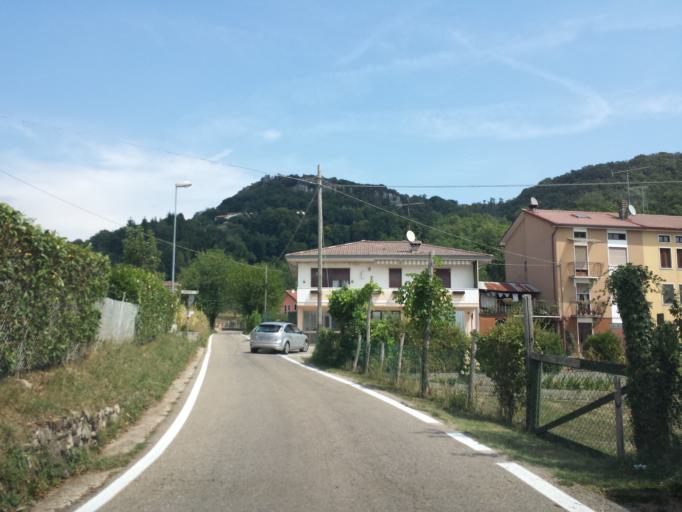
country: IT
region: Veneto
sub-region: Provincia di Vicenza
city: Valdagno
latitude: 45.6463
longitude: 11.3251
